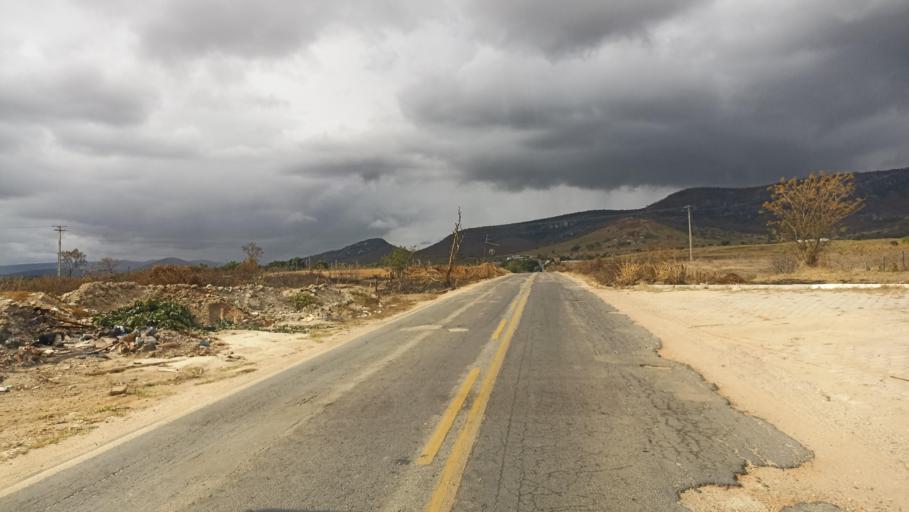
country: BR
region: Minas Gerais
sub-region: Itinga
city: Itinga
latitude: -16.6211
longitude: -41.7726
